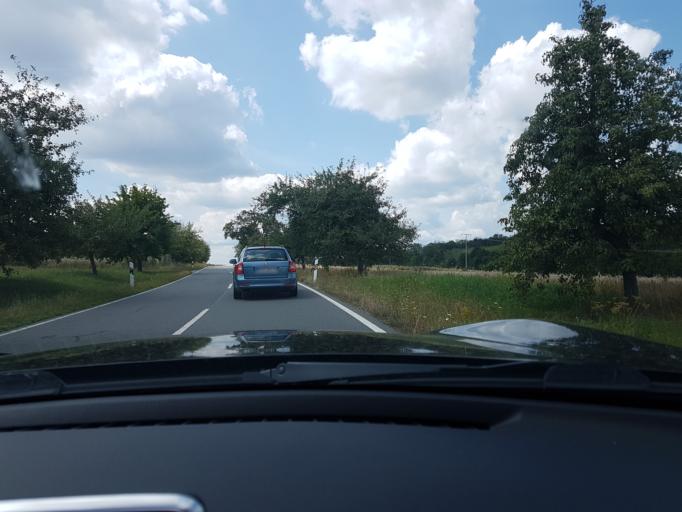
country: DE
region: Baden-Wuerttemberg
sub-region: Karlsruhe Region
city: Limbach
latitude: 49.4256
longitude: 9.2229
